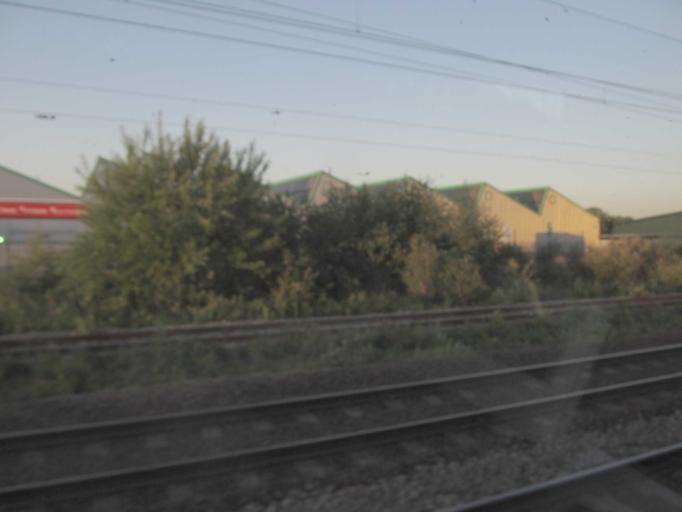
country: GB
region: England
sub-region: Lincolnshire
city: Grantham
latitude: 52.9027
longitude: -0.6378
